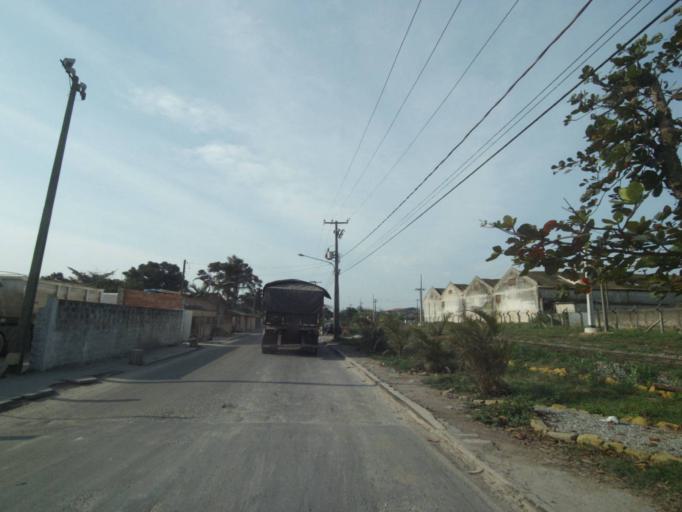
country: BR
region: Parana
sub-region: Paranagua
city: Paranagua
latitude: -25.5277
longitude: -48.5302
